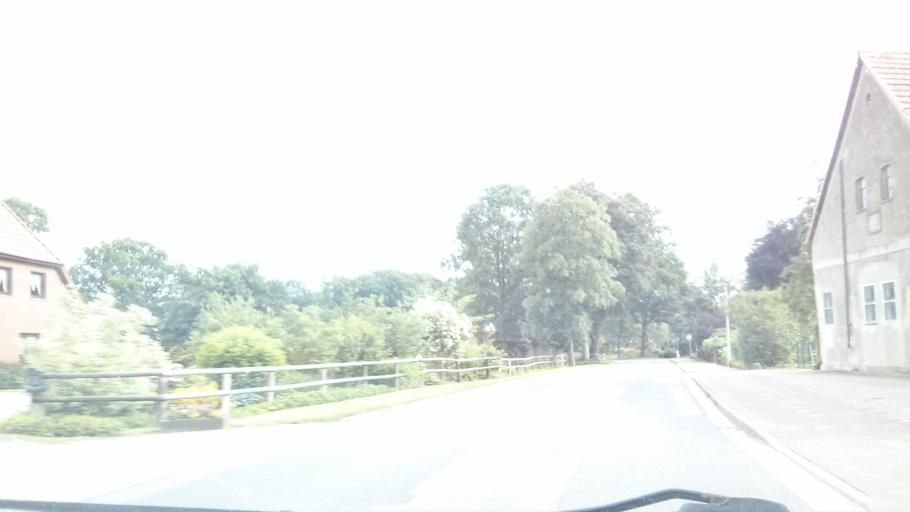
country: DE
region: Lower Saxony
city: Beverstedt
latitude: 53.4460
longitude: 8.8324
